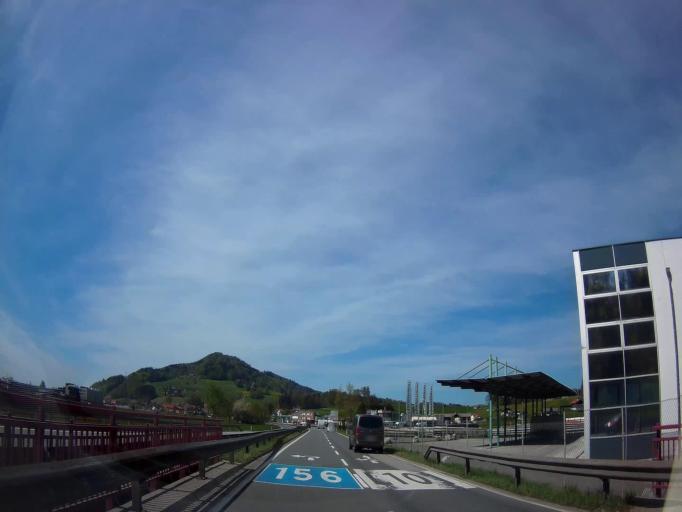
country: AT
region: Salzburg
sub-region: Politischer Bezirk Salzburg-Umgebung
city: Bergheim
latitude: 47.8406
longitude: 13.0534
